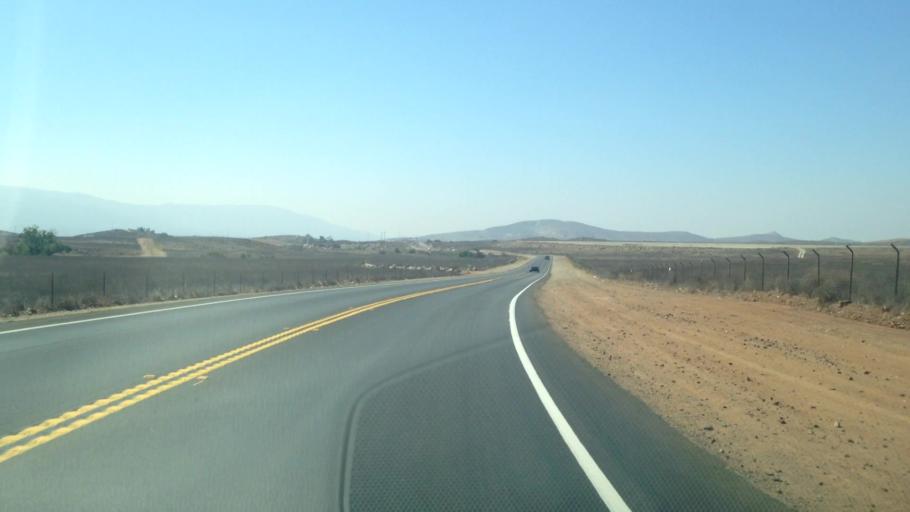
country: US
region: California
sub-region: Riverside County
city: El Cerrito
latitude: 33.8266
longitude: -117.4478
